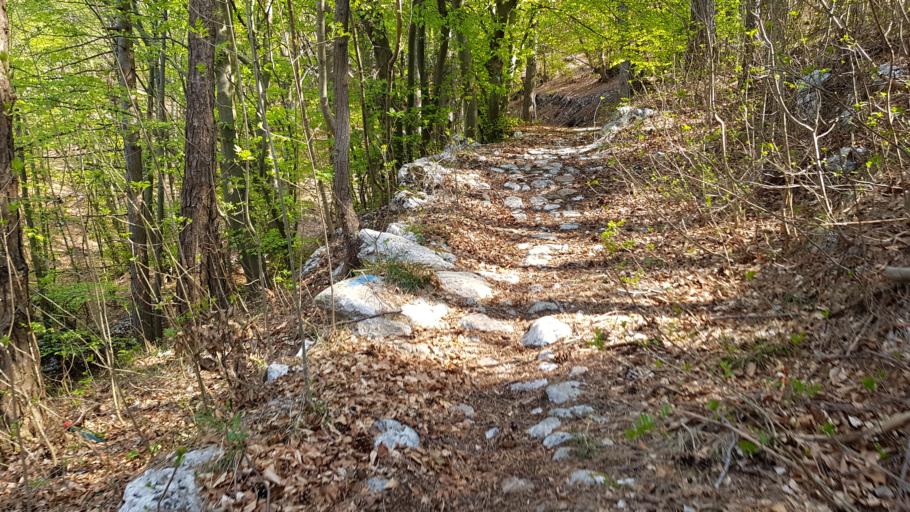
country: IT
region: Trentino-Alto Adige
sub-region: Provincia di Trento
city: Vezzano
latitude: 46.0743
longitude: 11.0084
